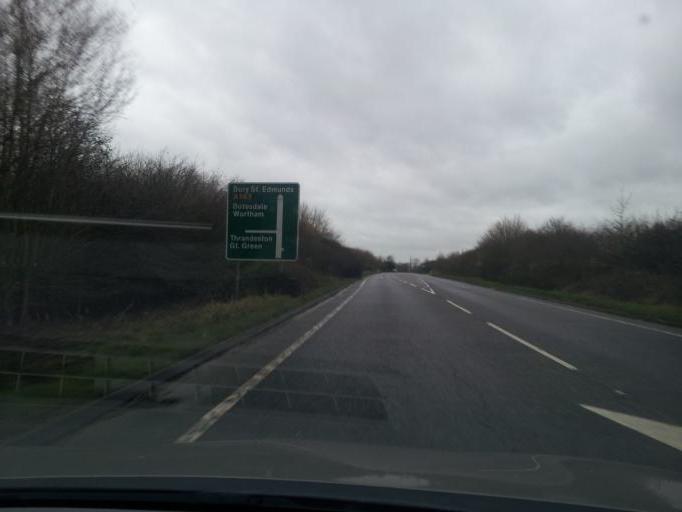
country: GB
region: England
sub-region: Norfolk
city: Diss
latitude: 52.3594
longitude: 1.1158
